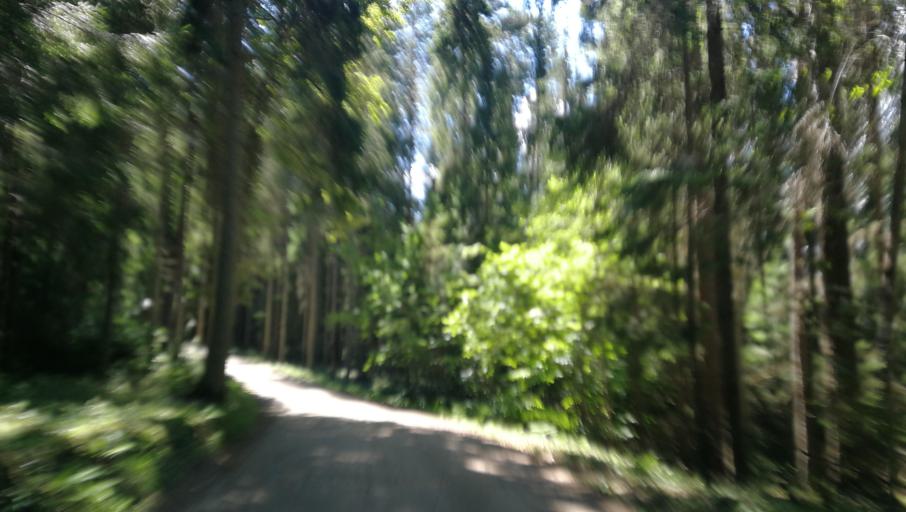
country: LV
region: Cesu Rajons
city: Cesis
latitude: 57.2886
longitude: 25.2119
